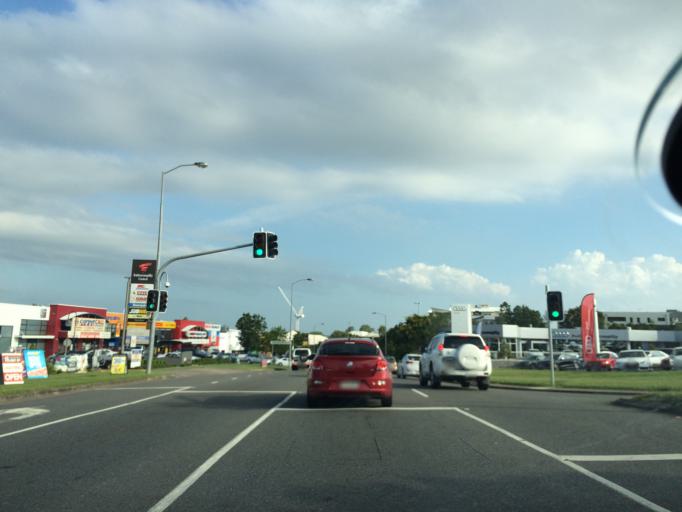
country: AU
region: Queensland
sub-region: Brisbane
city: Taringa
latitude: -27.4961
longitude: 152.9755
